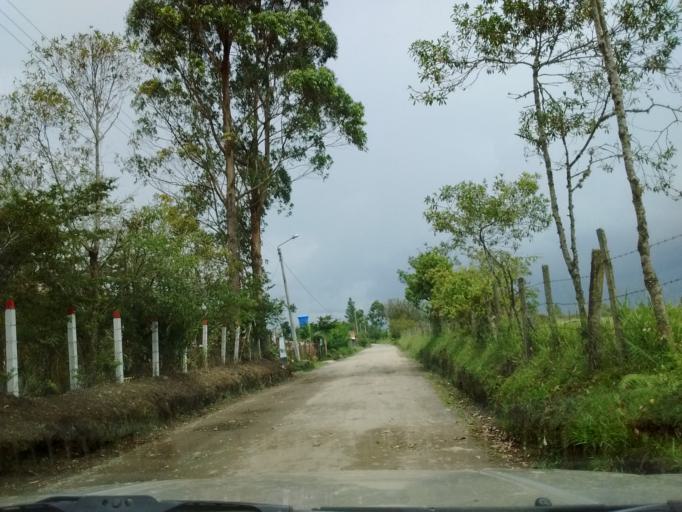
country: CO
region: Cauca
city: Cajibio
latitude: 2.5427
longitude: -76.6205
